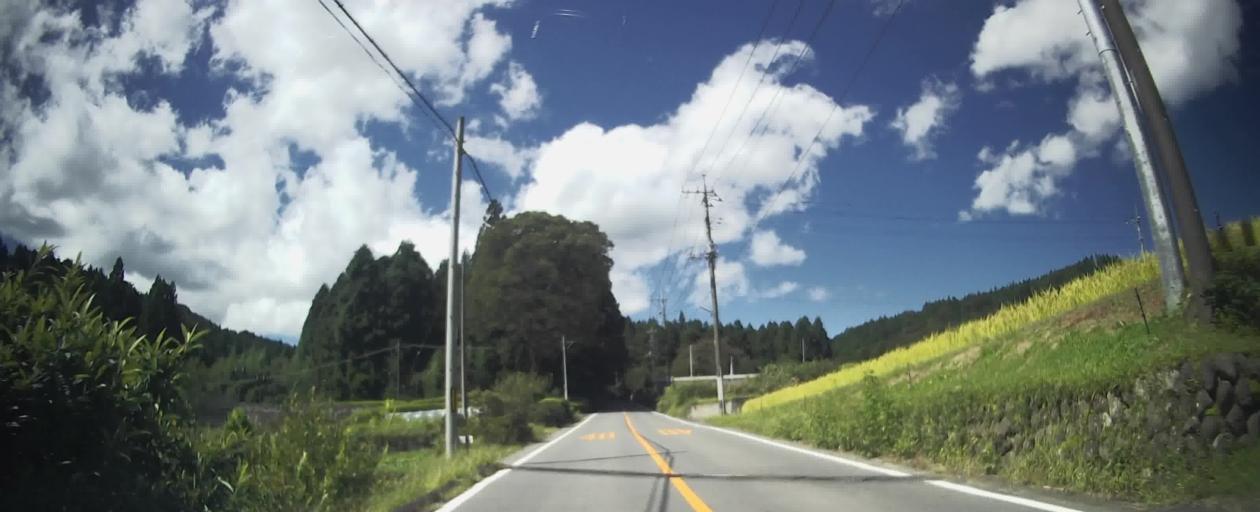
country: JP
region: Gunma
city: Kanekomachi
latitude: 36.4291
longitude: 138.9274
